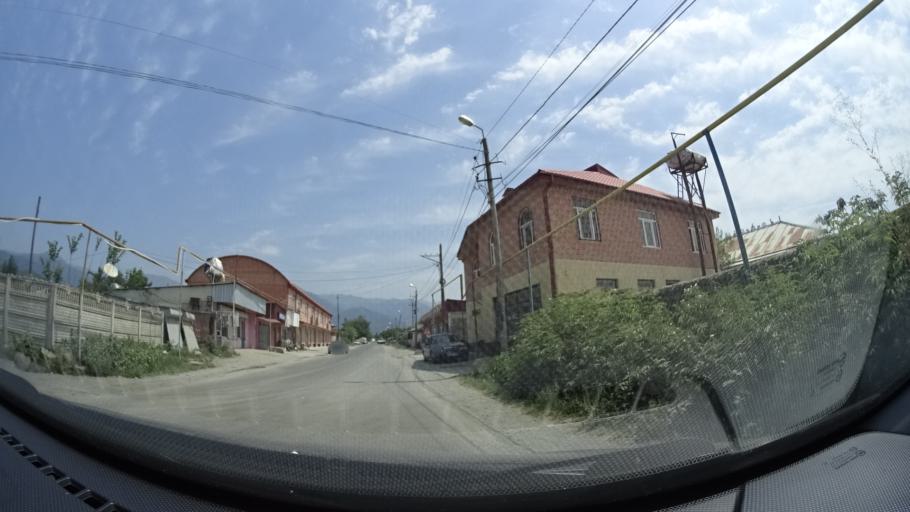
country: GE
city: Bagdadi
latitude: 41.8426
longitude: 46.1171
